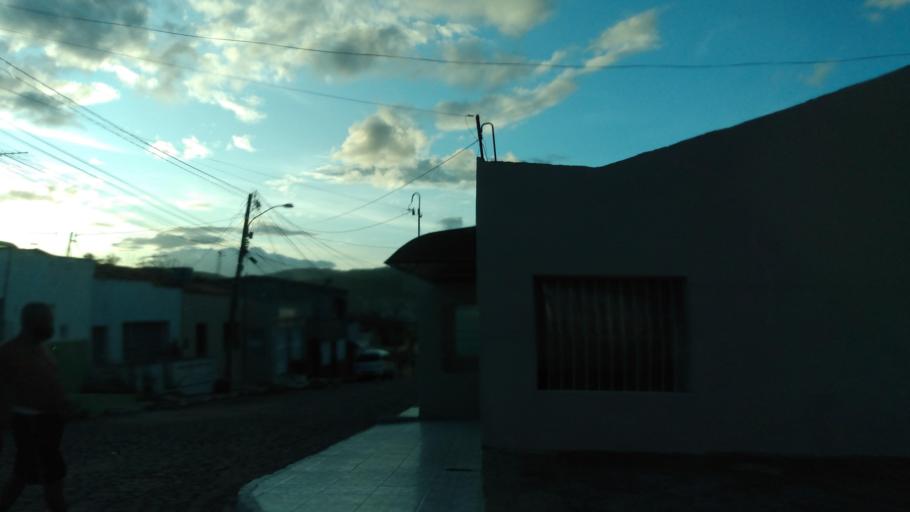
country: BR
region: Pernambuco
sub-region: Bezerros
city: Bezerros
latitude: -8.2402
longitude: -35.7510
